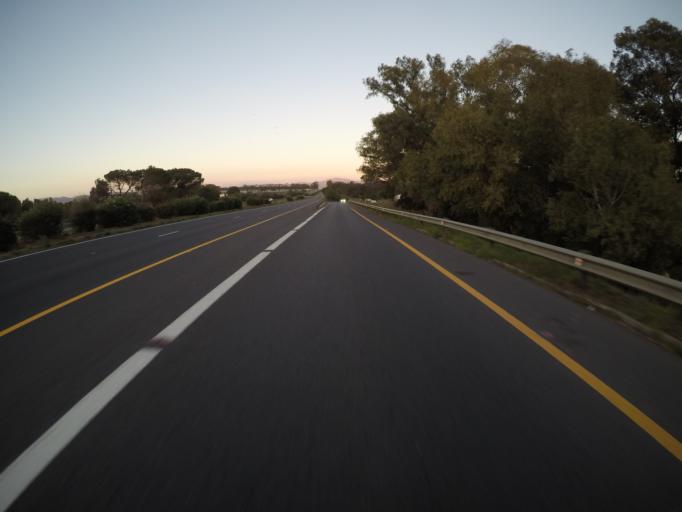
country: ZA
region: Western Cape
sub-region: Cape Winelands District Municipality
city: Paarl
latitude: -33.7992
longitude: 18.8679
